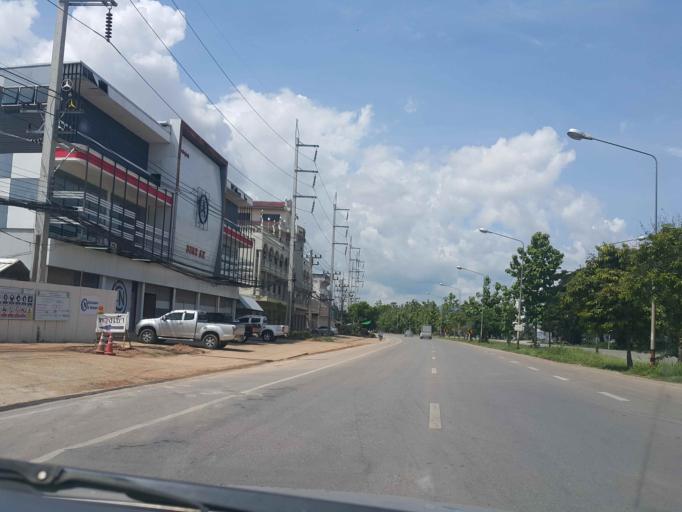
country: TH
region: Phayao
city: Phayao
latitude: 19.1555
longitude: 99.9136
